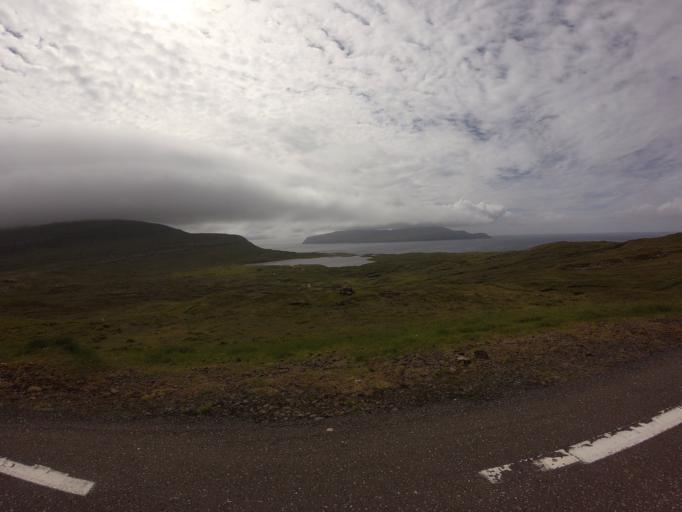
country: FO
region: Sandoy
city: Sandur
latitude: 61.8264
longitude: -6.7470
